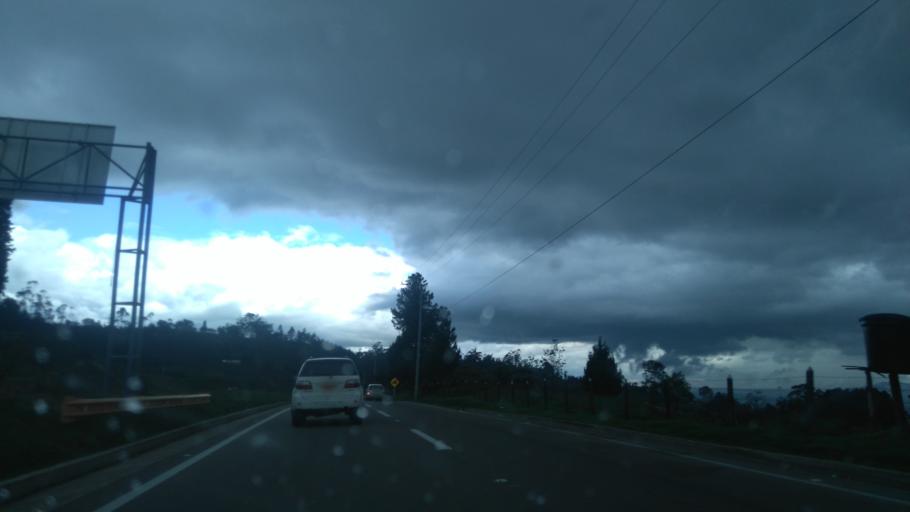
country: CO
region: Cundinamarca
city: El Rosal
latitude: 4.8729
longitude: -74.2923
